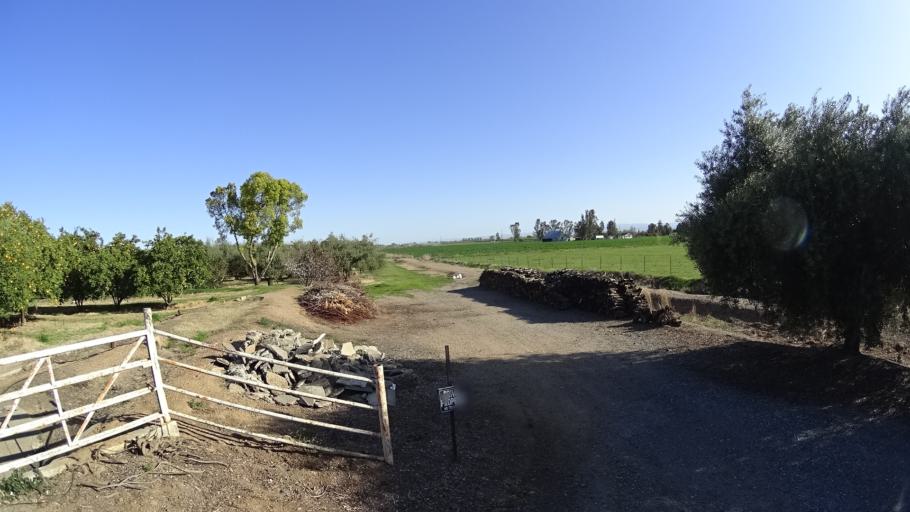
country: US
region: California
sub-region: Glenn County
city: Orland
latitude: 39.7636
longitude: -122.1134
